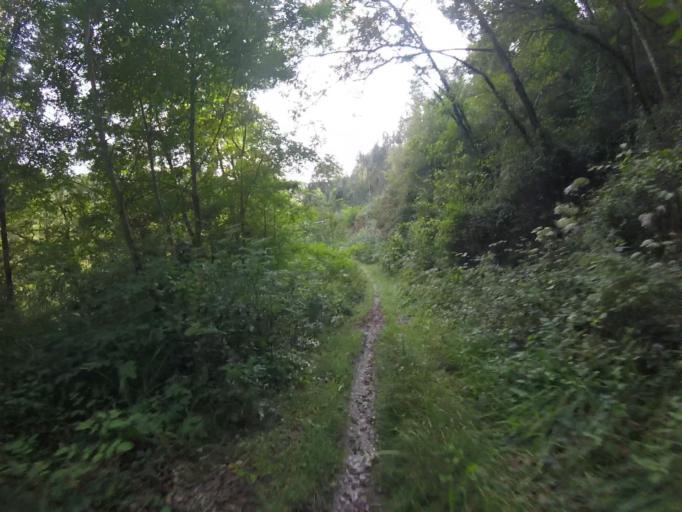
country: ES
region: Navarre
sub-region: Provincia de Navarra
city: Arano
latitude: 43.2278
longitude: -1.9336
